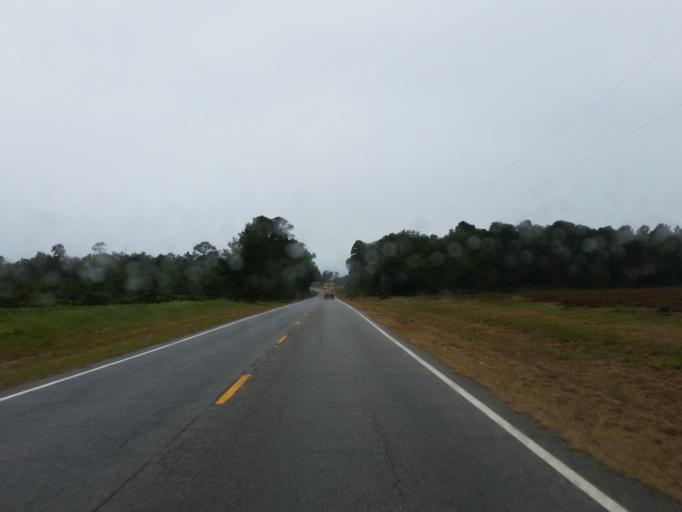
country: US
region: Georgia
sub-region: Berrien County
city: Nashville
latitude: 31.1143
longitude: -83.3035
